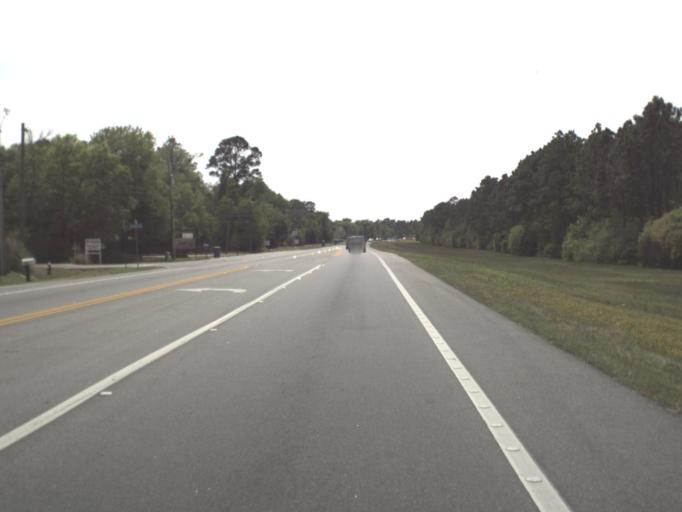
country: US
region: Florida
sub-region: Escambia County
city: Myrtle Grove
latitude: 30.4269
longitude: -87.3258
